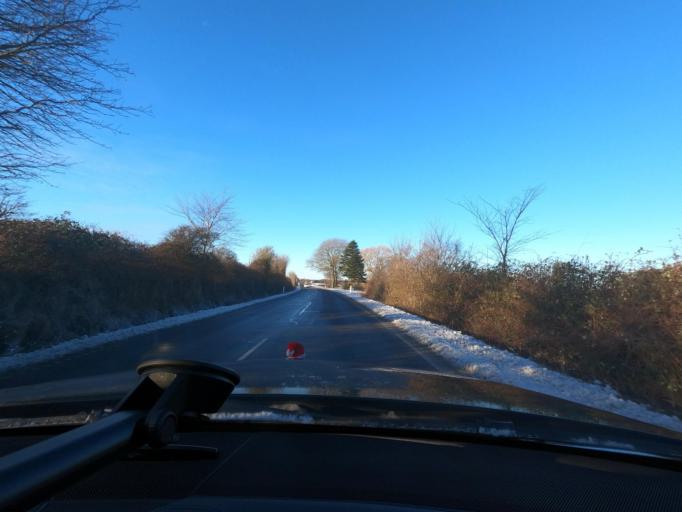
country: DK
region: South Denmark
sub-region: Sonderborg Kommune
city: Horuphav
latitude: 54.8637
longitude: 9.9653
